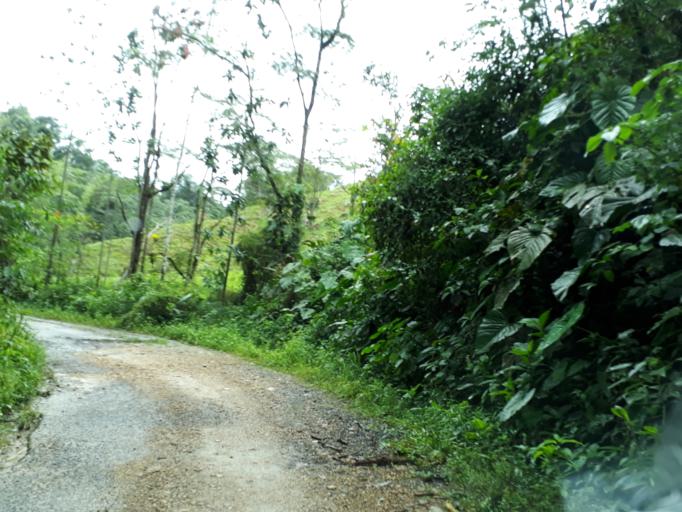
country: CO
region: Cundinamarca
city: Medina
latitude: 4.6855
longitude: -73.3127
